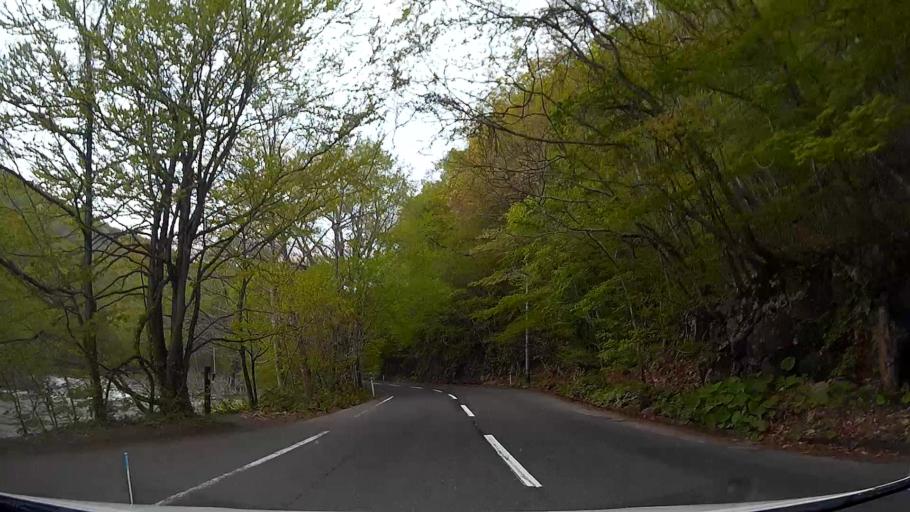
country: JP
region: Aomori
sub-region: Aomori Shi
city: Furudate
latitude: 40.5706
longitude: 140.9791
